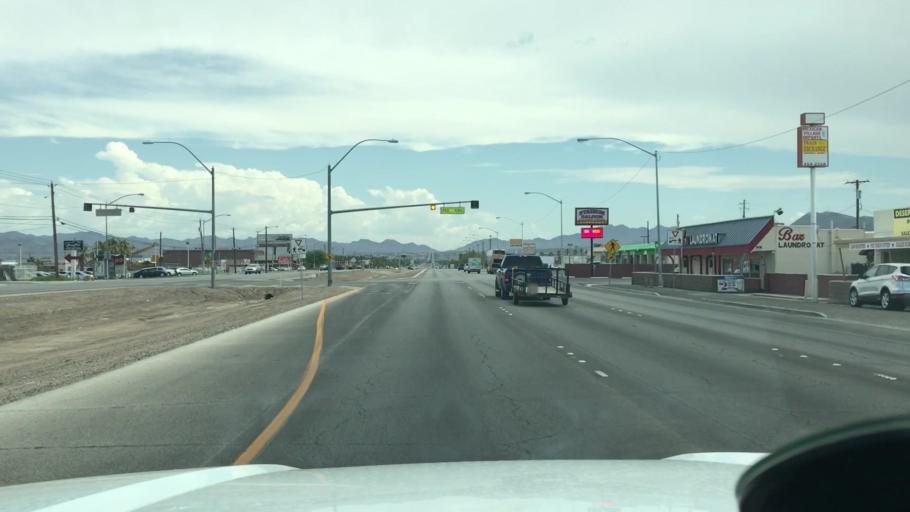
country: US
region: Nevada
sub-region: Clark County
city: Whitney
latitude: 36.0927
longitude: -115.0421
